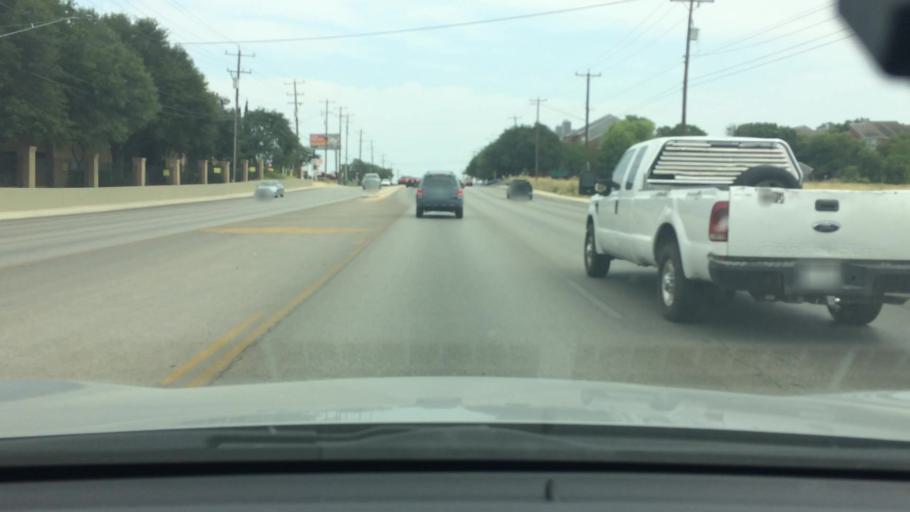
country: US
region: Texas
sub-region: Bexar County
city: Leon Valley
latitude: 29.4627
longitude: -98.6426
